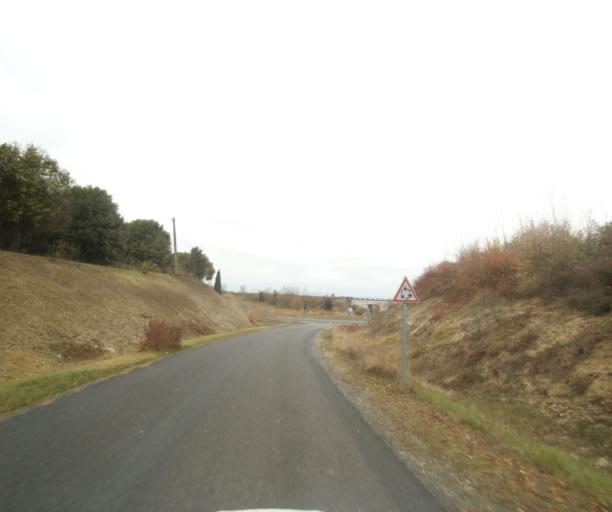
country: FR
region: Poitou-Charentes
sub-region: Departement de la Charente-Maritime
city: Saintes
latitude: 45.7435
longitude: -0.6751
